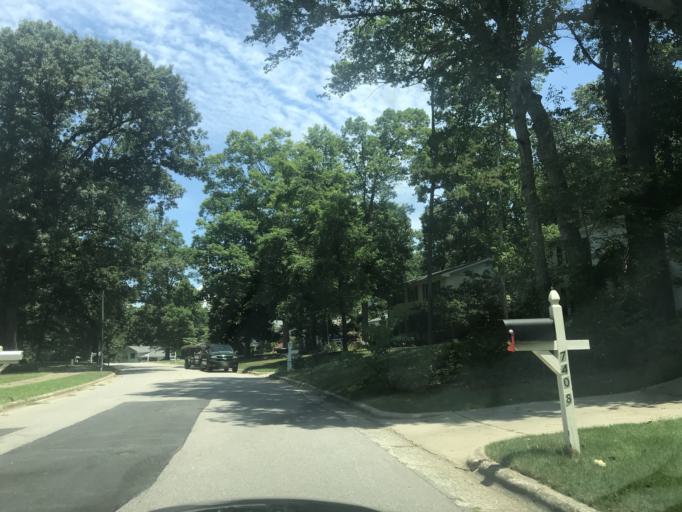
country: US
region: North Carolina
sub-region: Wake County
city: West Raleigh
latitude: 35.8889
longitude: -78.6217
